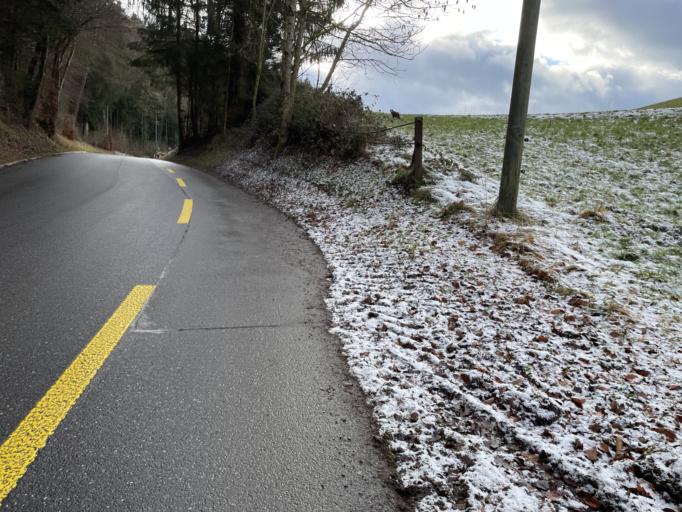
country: CH
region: Bern
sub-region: Thun District
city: Heimberg
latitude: 46.8076
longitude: 7.6107
